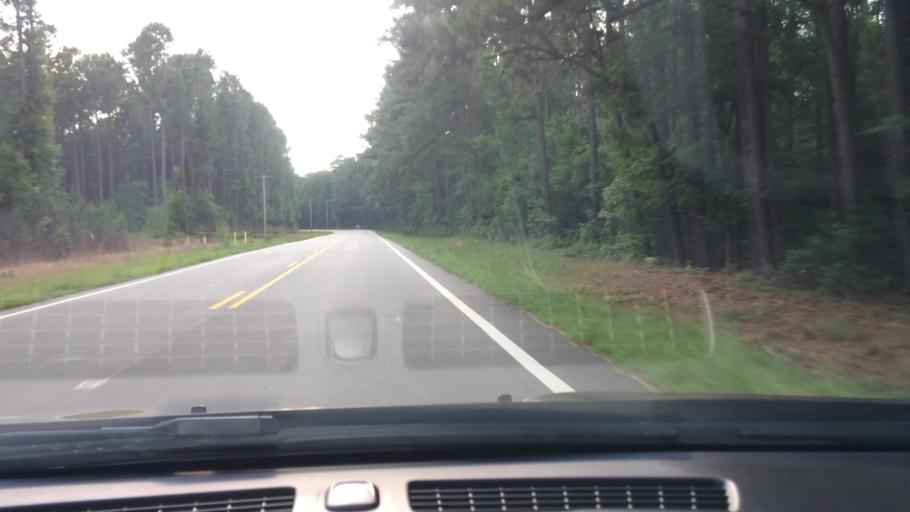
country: US
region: North Carolina
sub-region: Craven County
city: Vanceboro
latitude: 35.4191
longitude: -77.2488
